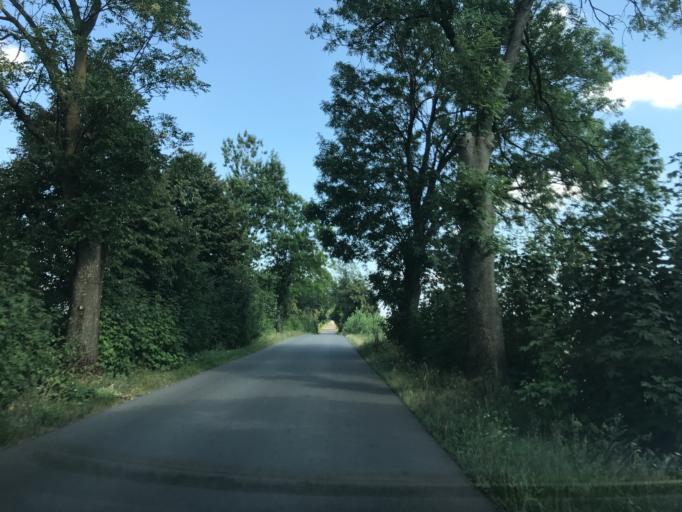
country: PL
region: Masovian Voivodeship
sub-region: Powiat zurominski
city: Lubowidz
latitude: 53.1741
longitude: 19.8767
